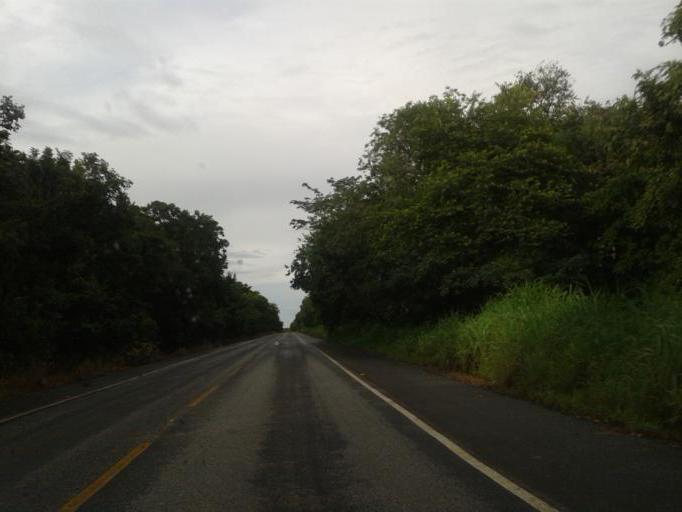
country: BR
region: Goias
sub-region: Mozarlandia
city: Mozarlandia
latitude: -14.8691
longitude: -50.5503
